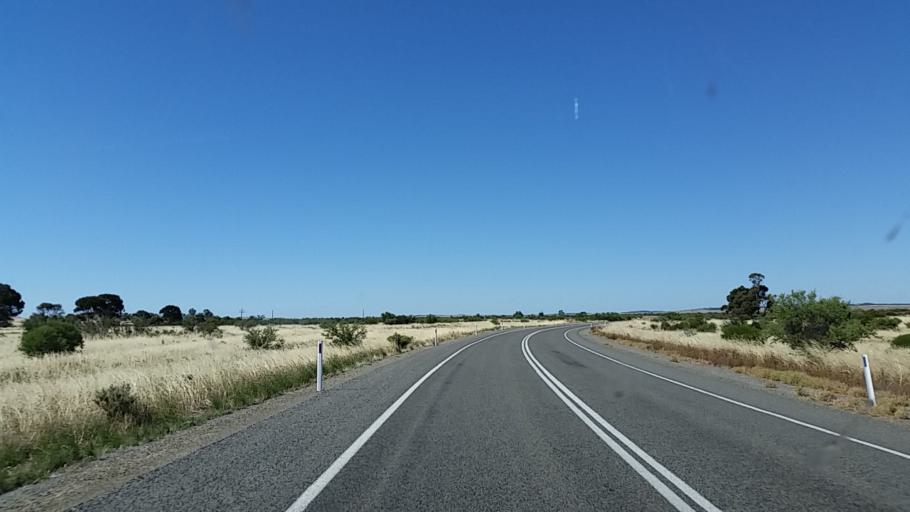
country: AU
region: South Australia
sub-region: Peterborough
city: Peterborough
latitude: -33.1733
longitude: 138.9097
